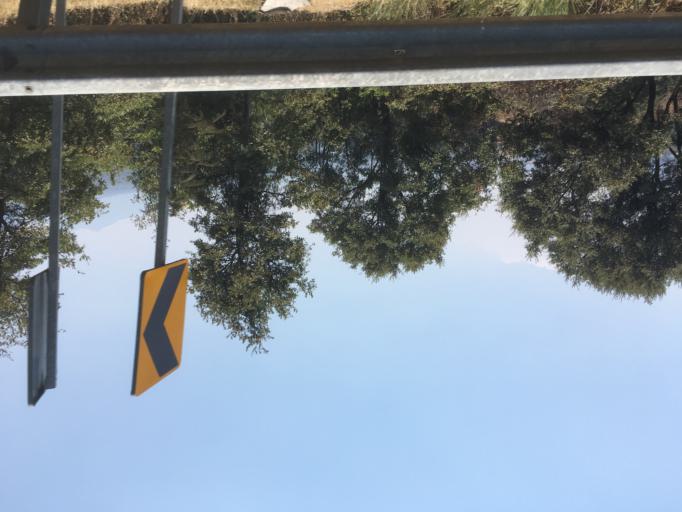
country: MX
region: Michoacan
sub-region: Morelia
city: Iratzio
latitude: 19.6266
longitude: -101.4596
